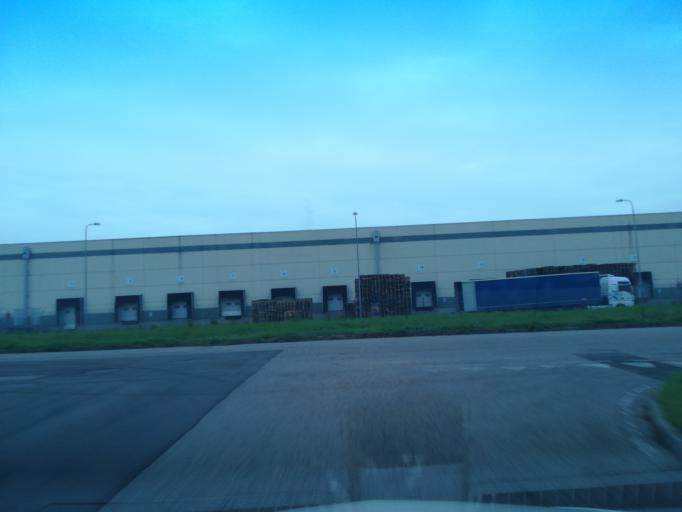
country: IT
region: Emilia-Romagna
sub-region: Provincia di Ravenna
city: Faenza
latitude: 44.3127
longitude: 11.9022
